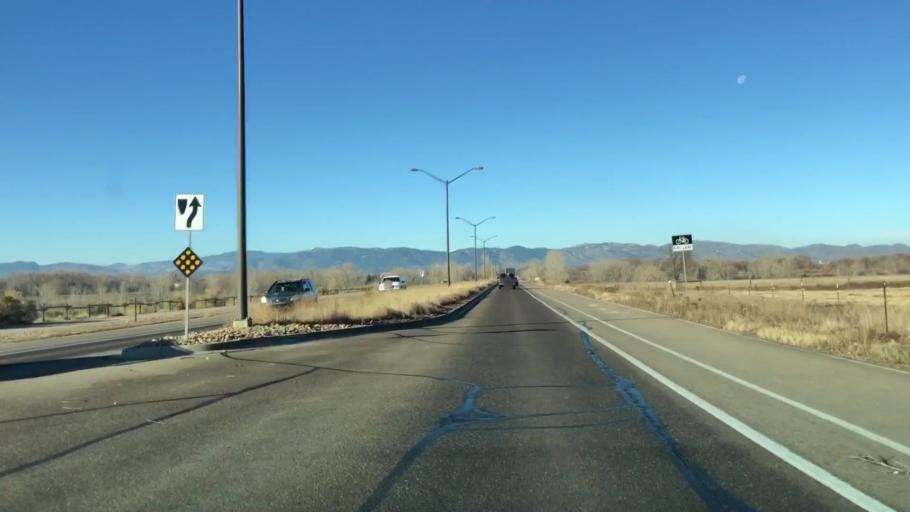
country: US
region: Colorado
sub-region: Larimer County
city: Fort Collins
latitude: 40.5665
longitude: -105.0170
